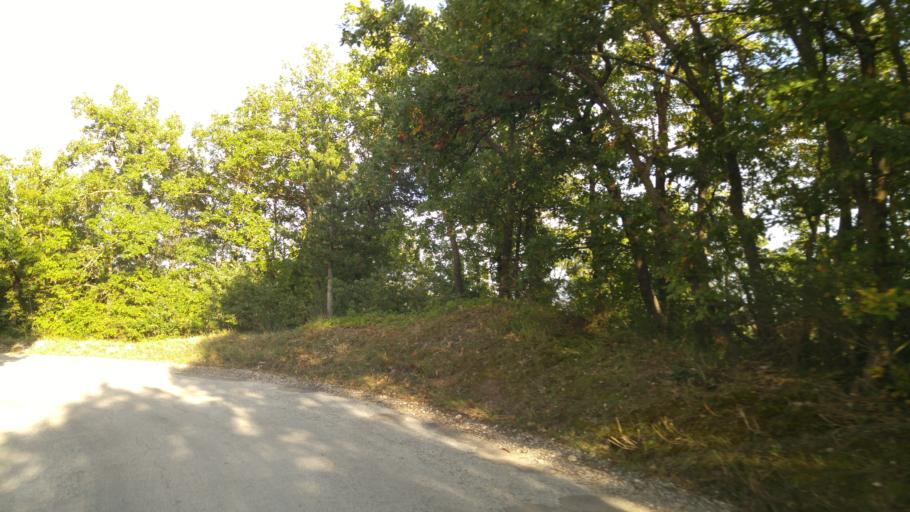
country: IT
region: The Marches
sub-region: Provincia di Pesaro e Urbino
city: Cagli
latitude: 43.5505
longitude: 12.6364
